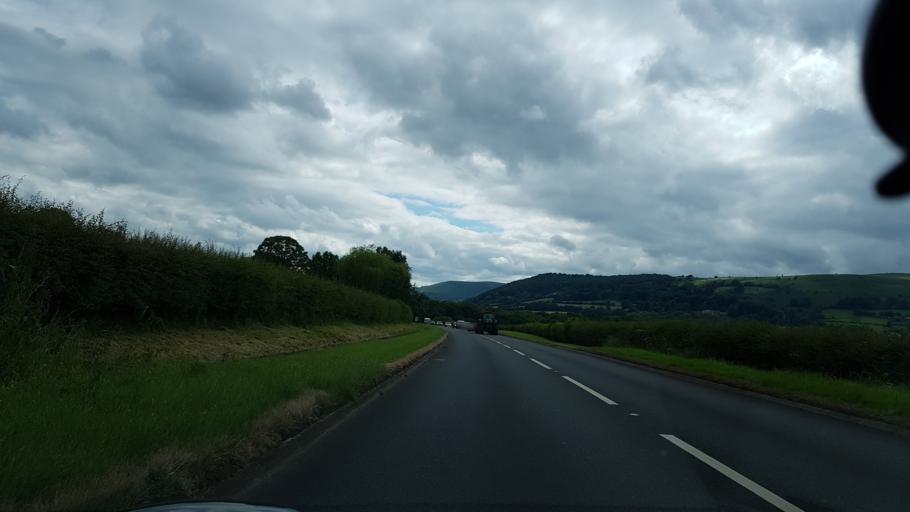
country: GB
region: Wales
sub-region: Monmouthshire
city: Abergavenny
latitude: 51.8621
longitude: -2.9957
